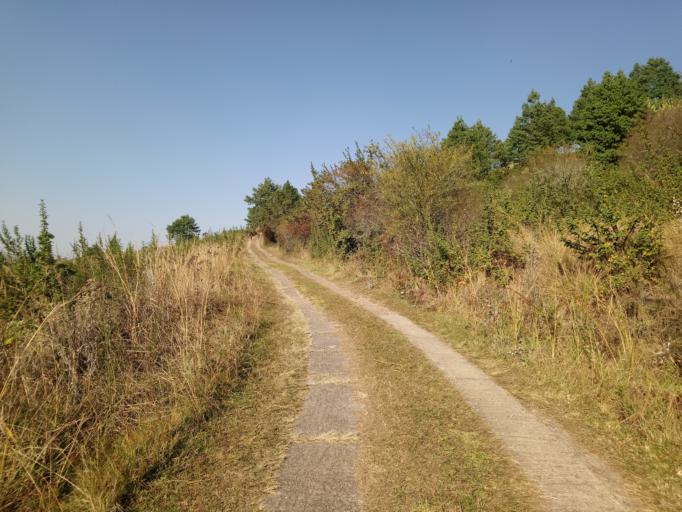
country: ZA
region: KwaZulu-Natal
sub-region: uMgungundlovu District Municipality
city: Mooirivier
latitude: -29.3328
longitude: 29.9211
